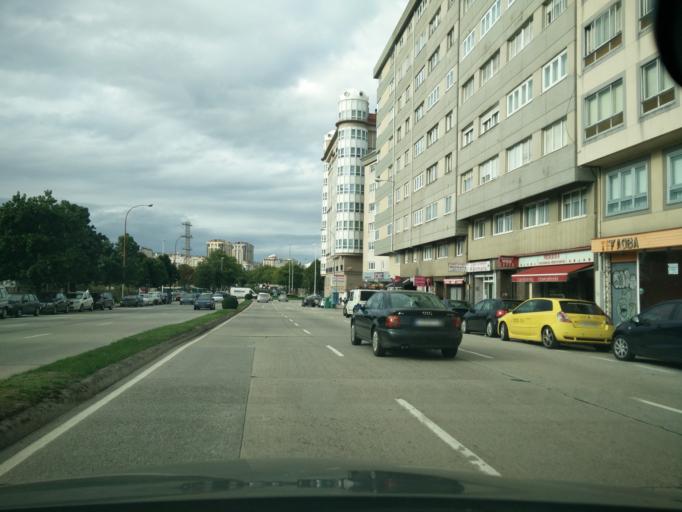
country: ES
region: Galicia
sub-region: Provincia da Coruna
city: A Coruna
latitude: 43.3669
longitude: -8.4246
